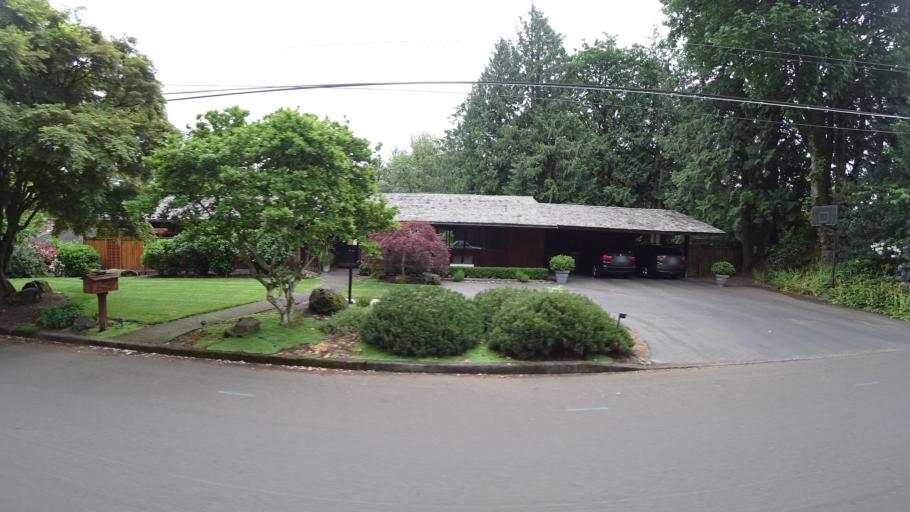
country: US
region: Oregon
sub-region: Washington County
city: Raleigh Hills
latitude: 45.4810
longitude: -122.7503
